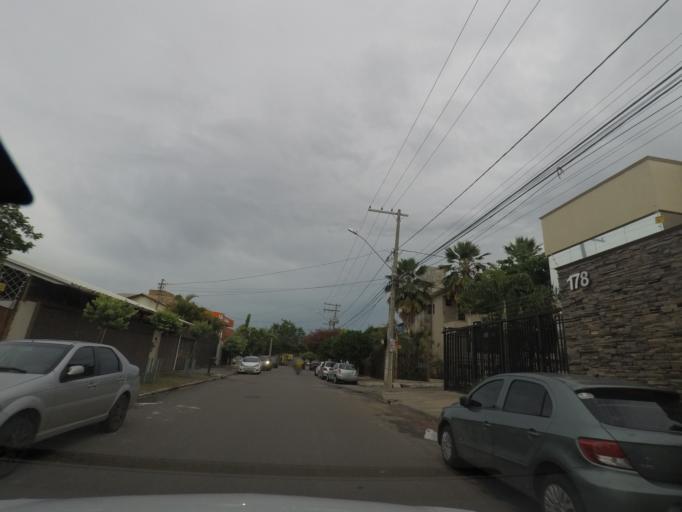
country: BR
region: Goias
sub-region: Goiania
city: Goiania
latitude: -16.6939
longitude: -49.2481
